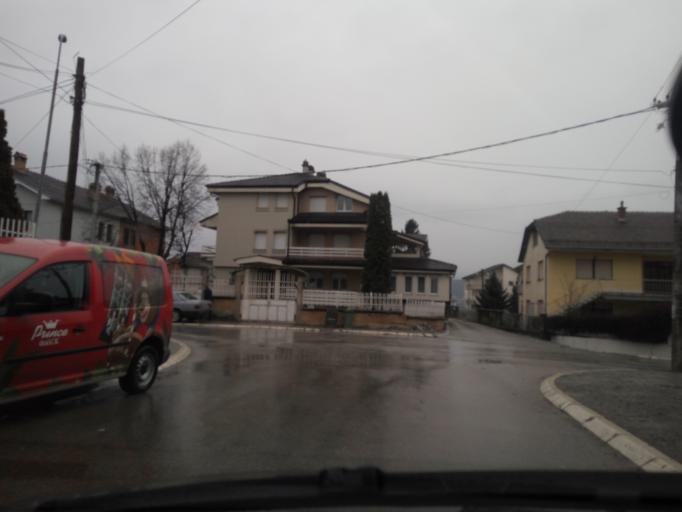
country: XK
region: Gjakova
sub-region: Komuna e Gjakoves
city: Gjakove
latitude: 42.3688
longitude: 20.4408
